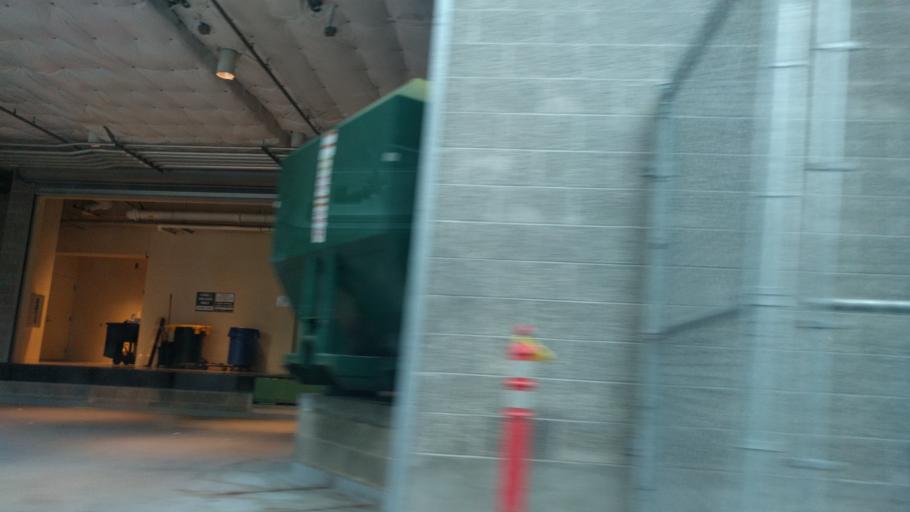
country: US
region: Washington
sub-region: King County
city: Seattle
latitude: 47.6240
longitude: -122.3353
